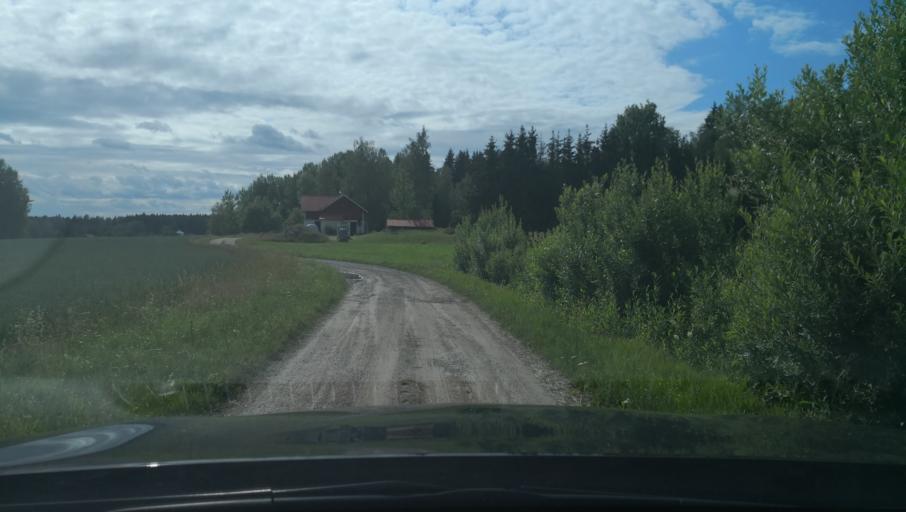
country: SE
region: Vaestmanland
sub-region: Kopings Kommun
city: Koping
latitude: 59.6403
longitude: 16.0694
